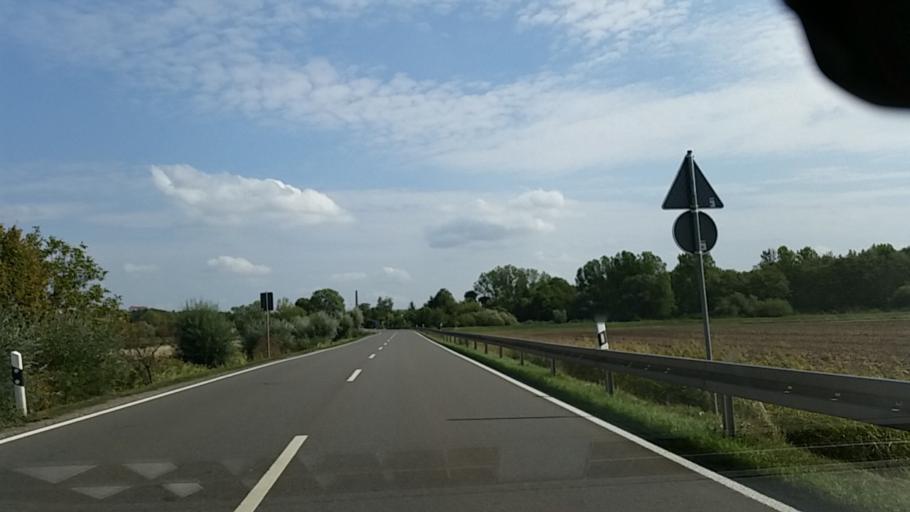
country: DE
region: Thuringia
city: Artern
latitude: 51.3625
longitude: 11.2792
